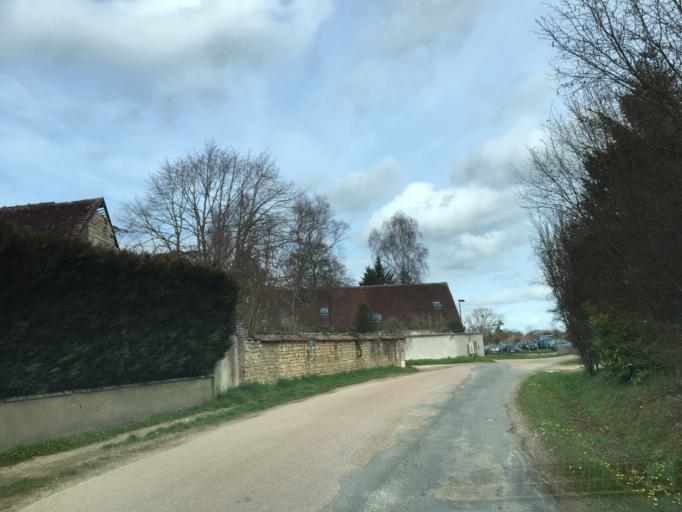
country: FR
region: Bourgogne
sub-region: Departement de l'Yonne
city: Fleury-la-Vallee
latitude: 47.8610
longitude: 3.4082
